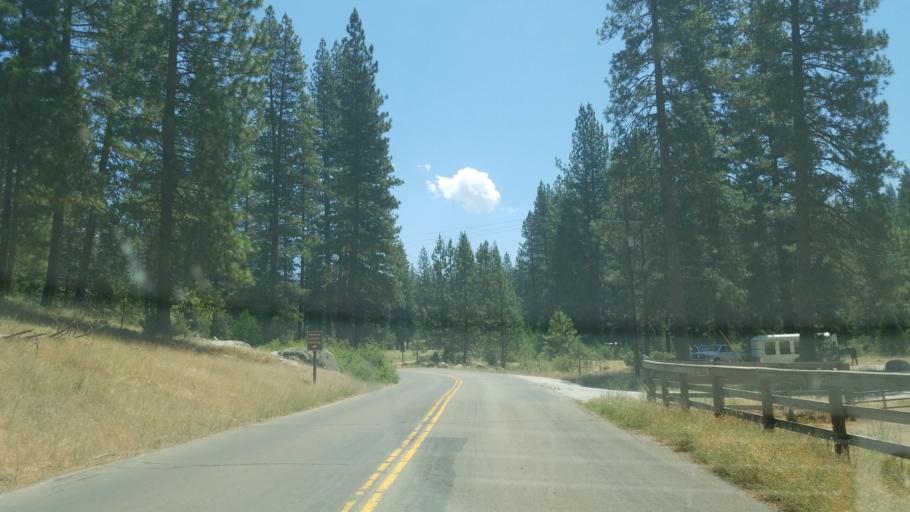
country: US
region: California
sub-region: Madera County
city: Ahwahnee
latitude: 37.5399
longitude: -119.6556
